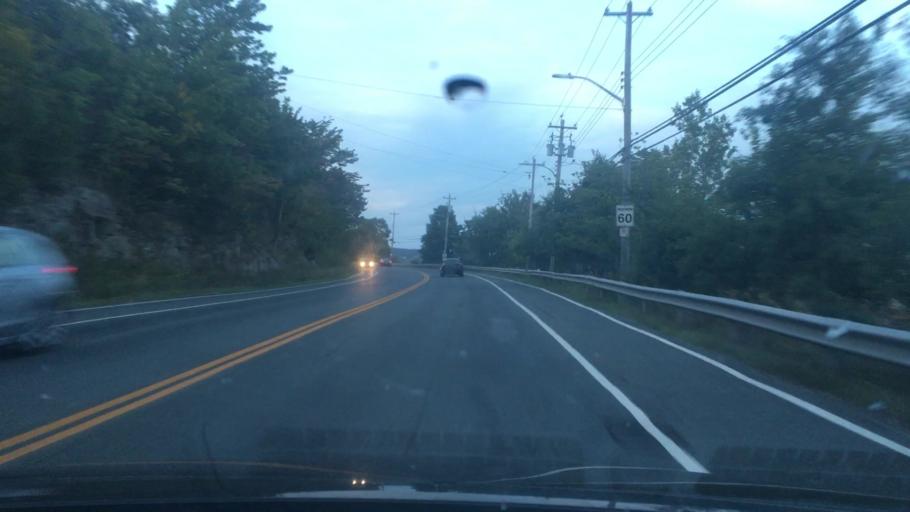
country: CA
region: Nova Scotia
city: Dartmouth
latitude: 44.6853
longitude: -63.6600
